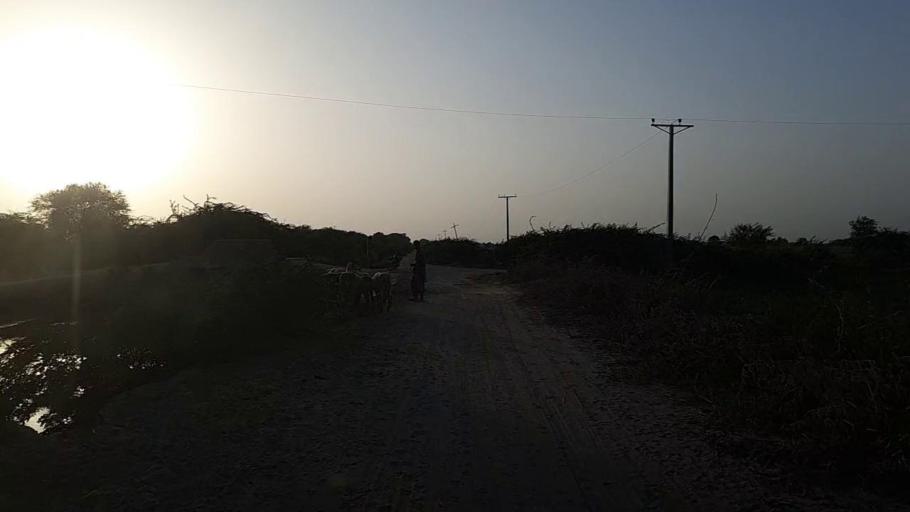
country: PK
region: Sindh
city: Kario
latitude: 24.7088
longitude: 68.4625
